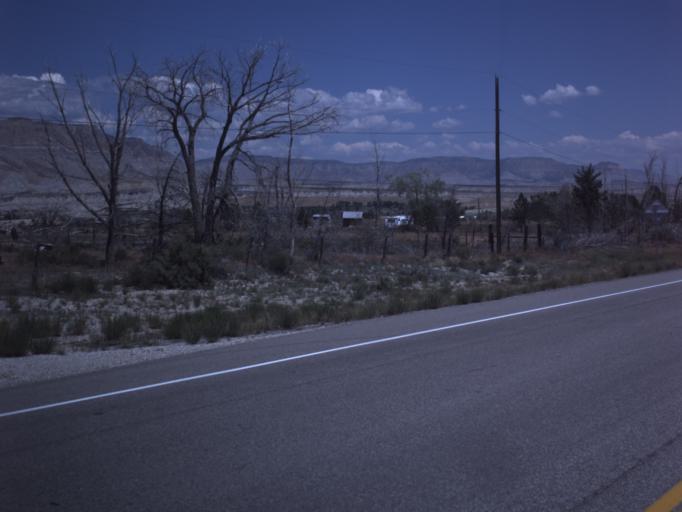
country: US
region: Utah
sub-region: Emery County
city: Ferron
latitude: 39.1306
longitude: -111.1013
